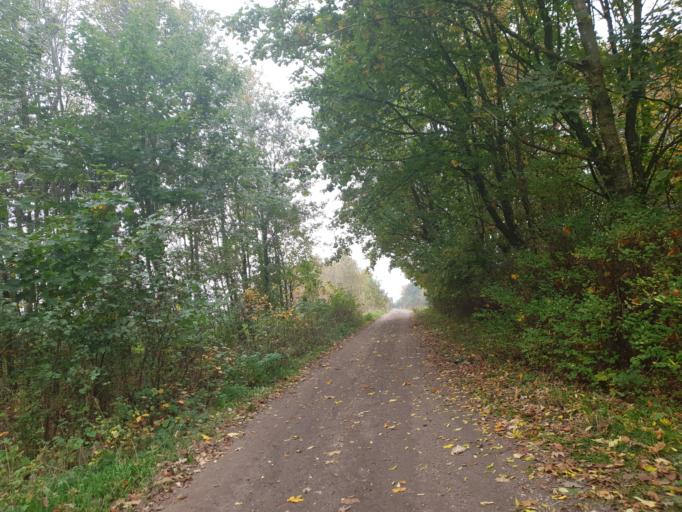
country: DK
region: Central Jutland
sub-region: Hedensted Kommune
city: Hedensted
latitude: 55.7959
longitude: 9.6829
